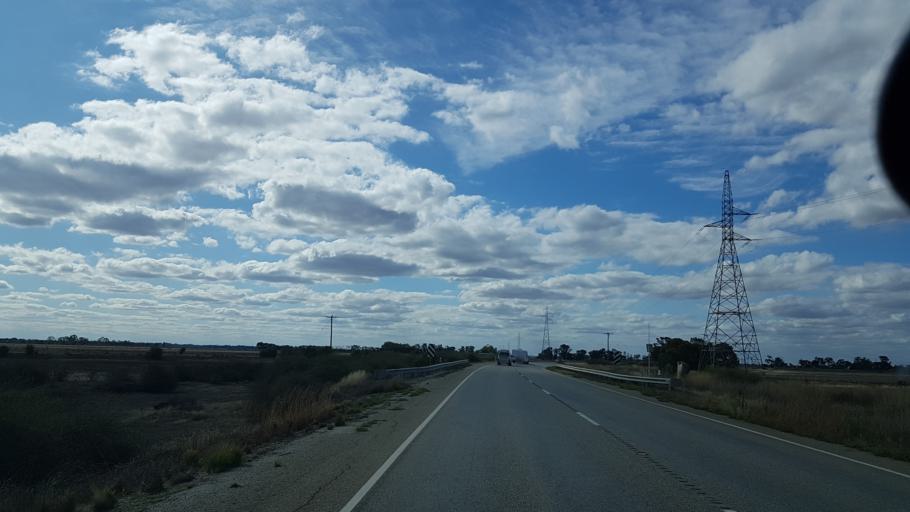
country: AU
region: Victoria
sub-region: Swan Hill
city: Swan Hill
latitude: -35.8653
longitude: 143.9350
